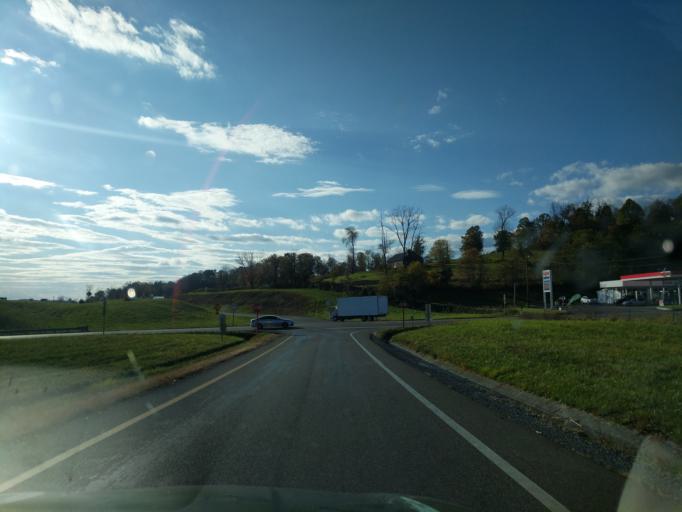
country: US
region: Virginia
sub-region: Washington County
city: Glade Spring
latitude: 36.7726
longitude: -81.7803
